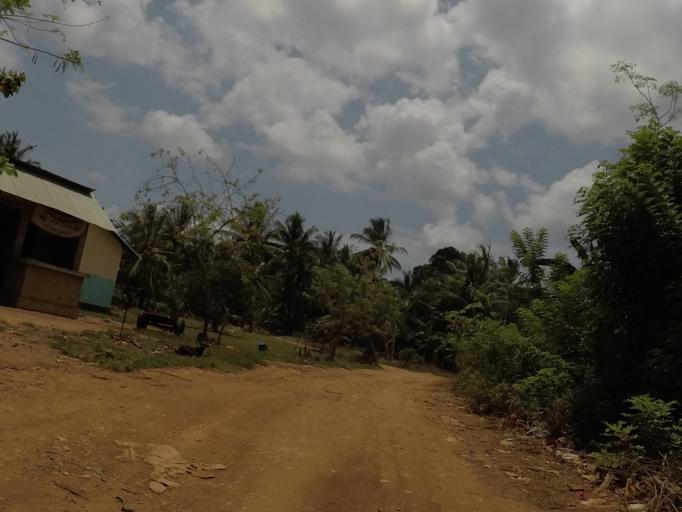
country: TZ
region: Zanzibar Central/South
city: Koani
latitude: -6.1850
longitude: 39.3105
